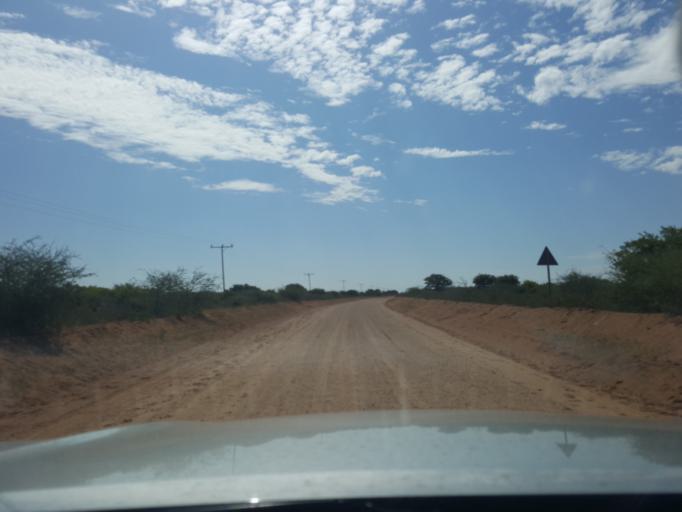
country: BW
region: Kweneng
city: Khudumelapye
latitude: -23.8481
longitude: 24.8660
